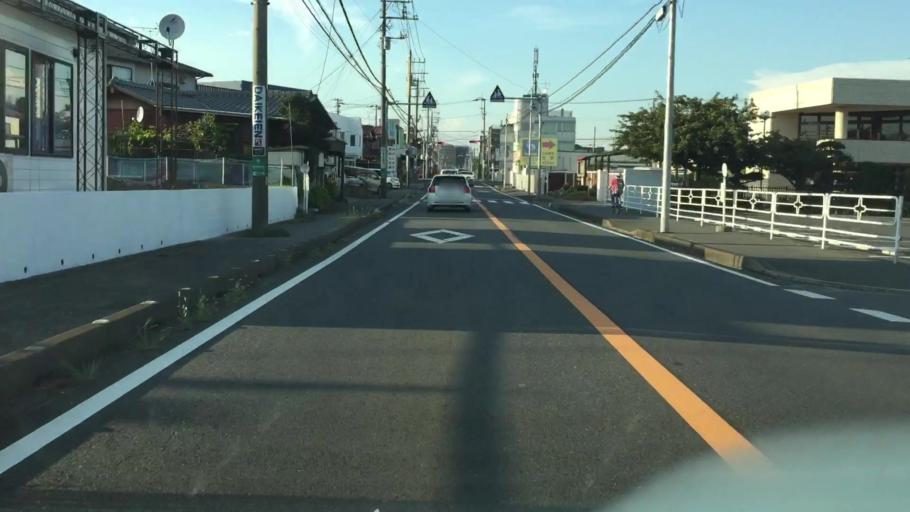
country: JP
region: Chiba
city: Funabashi
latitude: 35.7546
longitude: 139.9987
